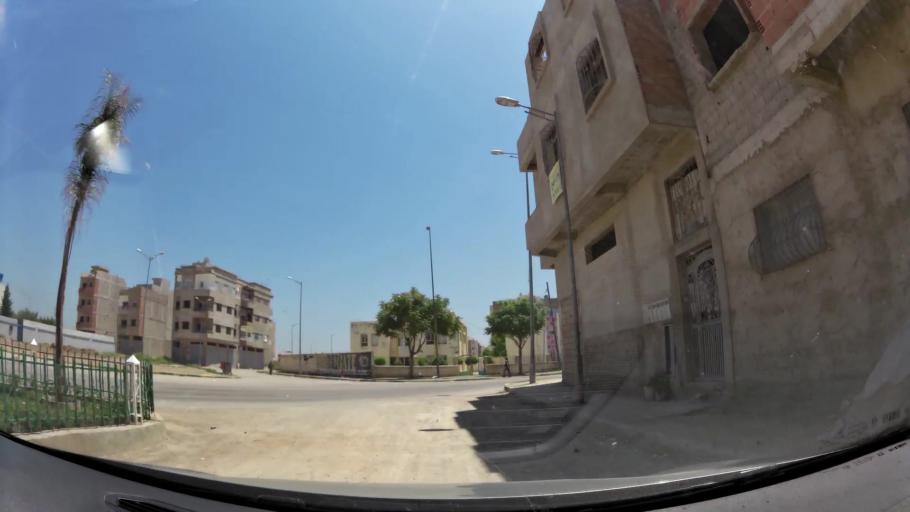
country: MA
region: Fes-Boulemane
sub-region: Fes
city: Fes
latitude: 34.0344
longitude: -5.0437
